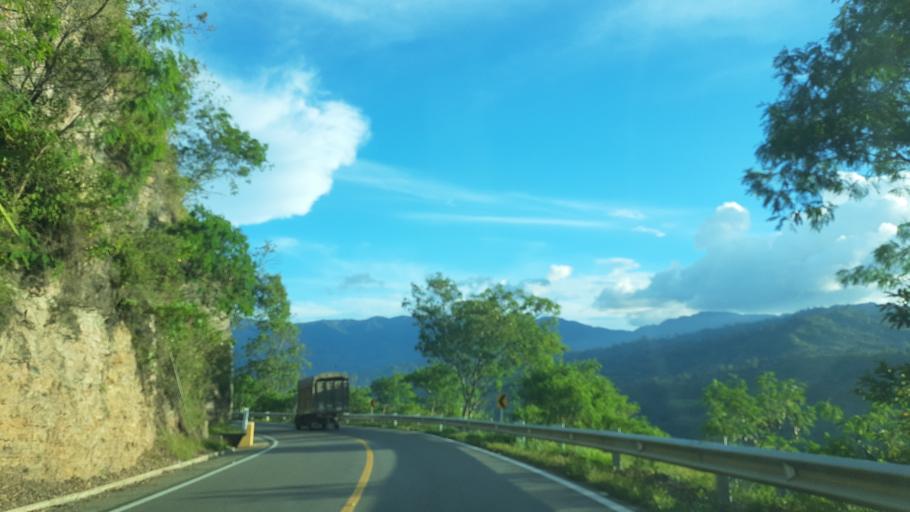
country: CO
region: Boyaca
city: Guateque
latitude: 5.0032
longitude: -73.5067
